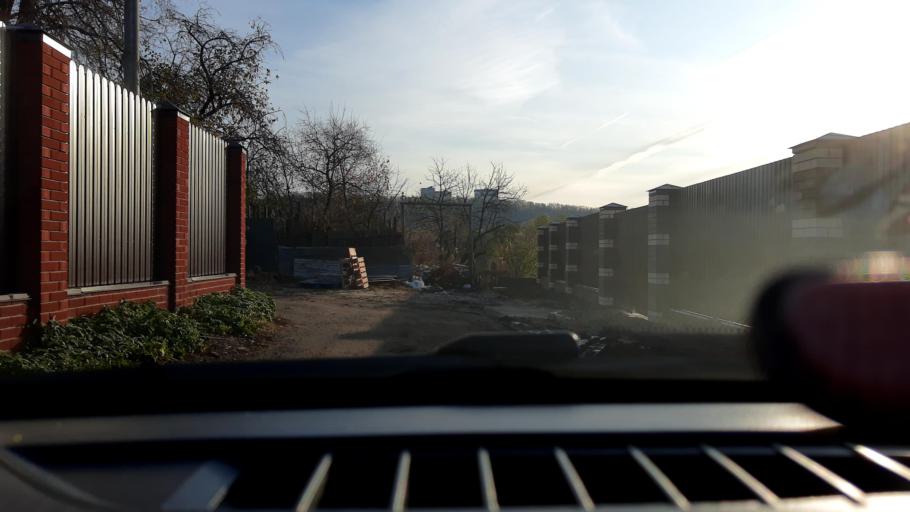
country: RU
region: Nizjnij Novgorod
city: Nizhniy Novgorod
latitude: 56.2708
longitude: 43.9544
